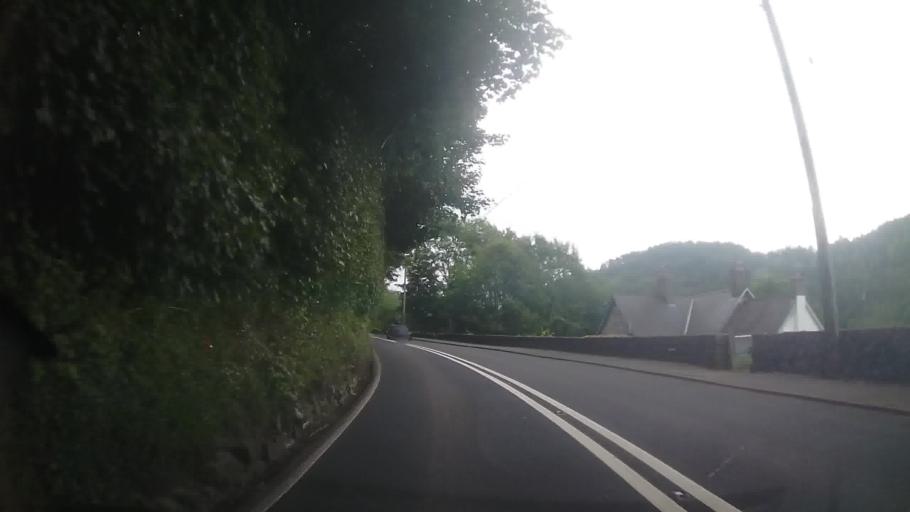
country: GB
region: Wales
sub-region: Conwy
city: Betws-y-Coed
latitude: 53.0712
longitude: -3.7864
